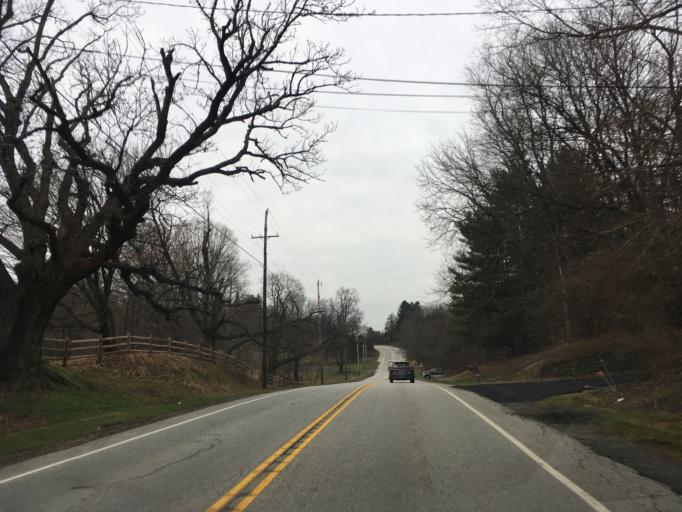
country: US
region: Delaware
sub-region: New Castle County
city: Greenville
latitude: 39.8401
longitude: -75.6300
